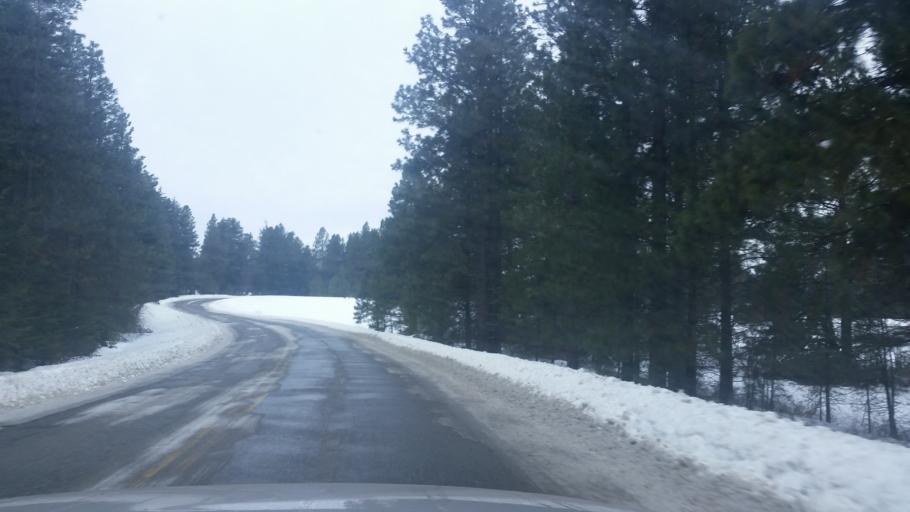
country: US
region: Washington
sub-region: Kittitas County
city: Cle Elum
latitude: 47.1588
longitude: -120.8399
